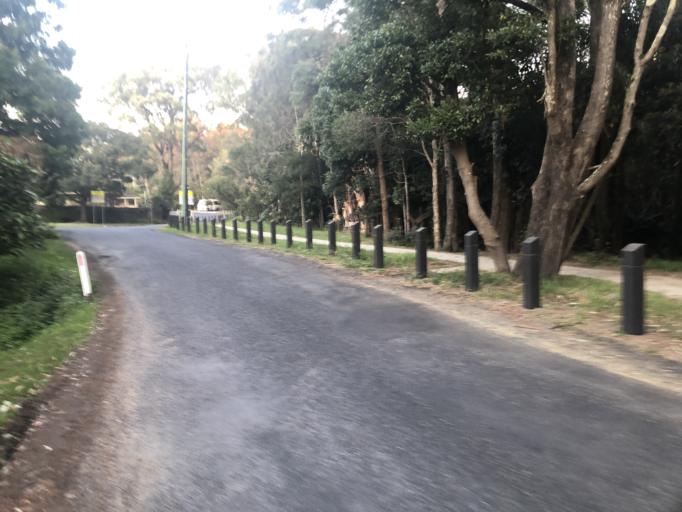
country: AU
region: New South Wales
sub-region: Coffs Harbour
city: Coffs Harbour
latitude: -30.2982
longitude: 153.1215
